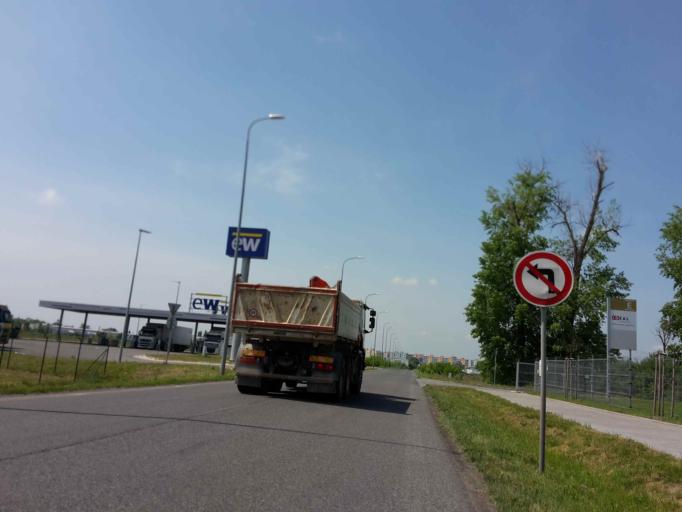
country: SK
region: Bratislavsky
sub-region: Okres Malacky
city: Malacky
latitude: 48.4217
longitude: 17.0336
